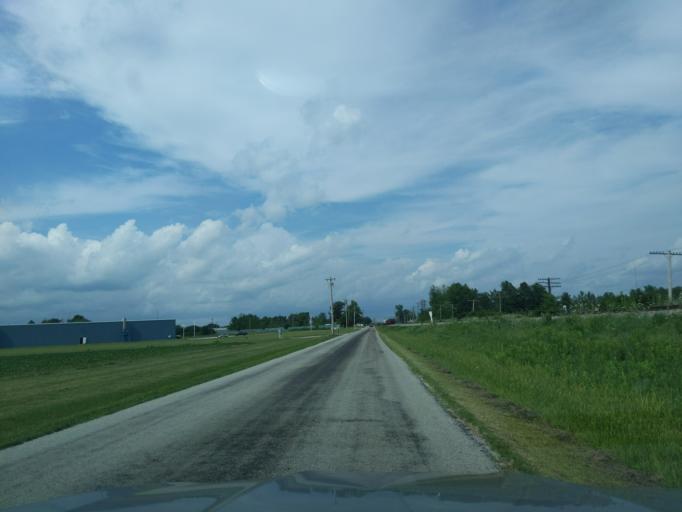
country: US
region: Indiana
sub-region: Ripley County
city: Osgood
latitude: 39.1215
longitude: -85.3005
